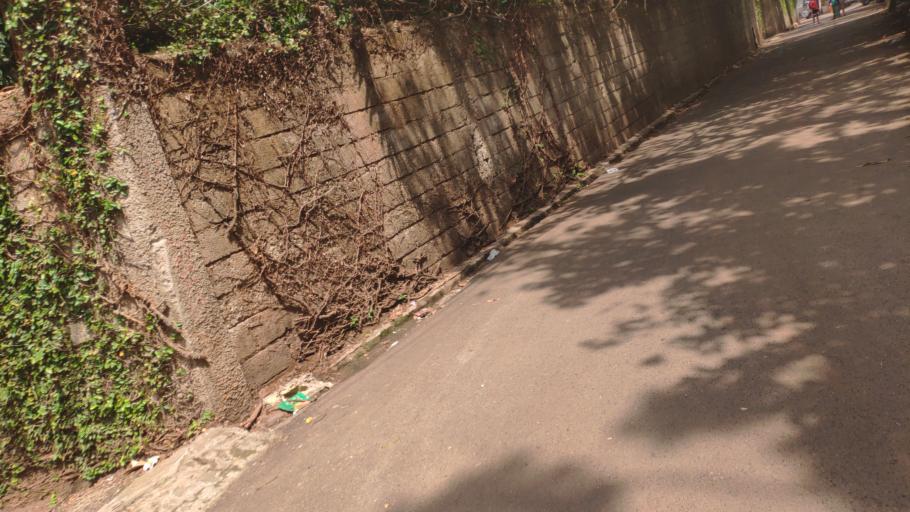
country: ID
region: Jakarta Raya
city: Jakarta
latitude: -6.2679
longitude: 106.8273
